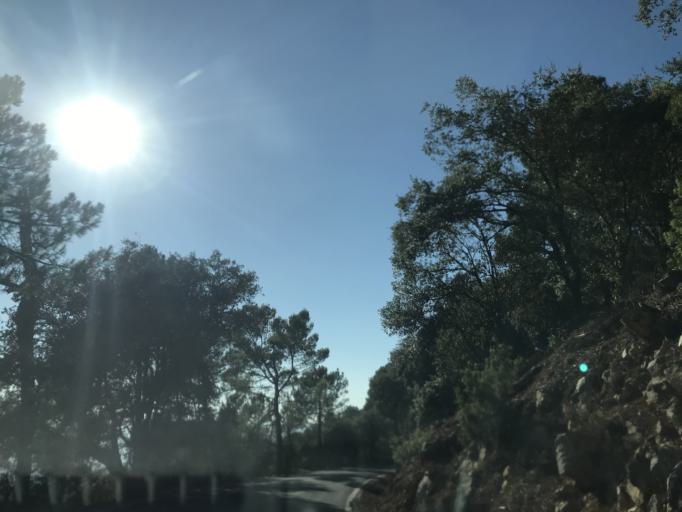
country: ES
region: Andalusia
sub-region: Provincia de Jaen
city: La Iruela
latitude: 37.9519
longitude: -2.9416
